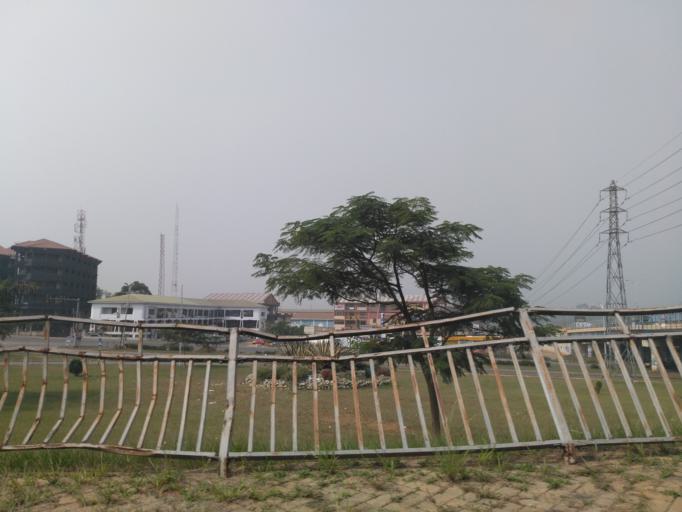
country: GH
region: Ashanti
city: Kumasi
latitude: 6.6686
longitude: -1.6051
